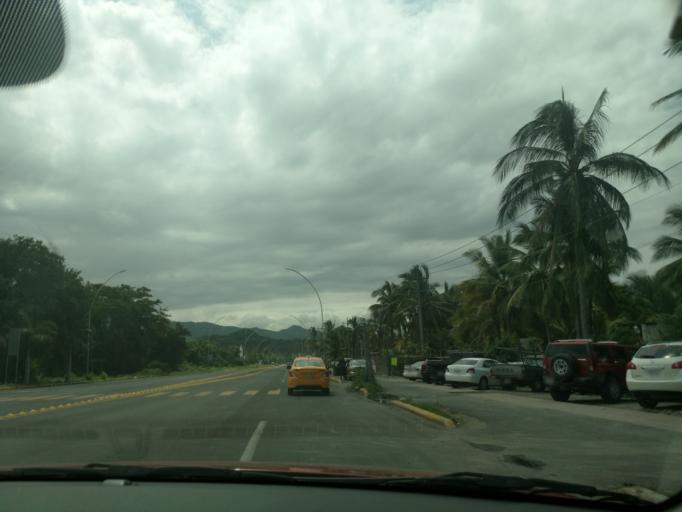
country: MX
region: Nayarit
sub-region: San Blas
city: Aticama
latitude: 21.5035
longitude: -105.2056
